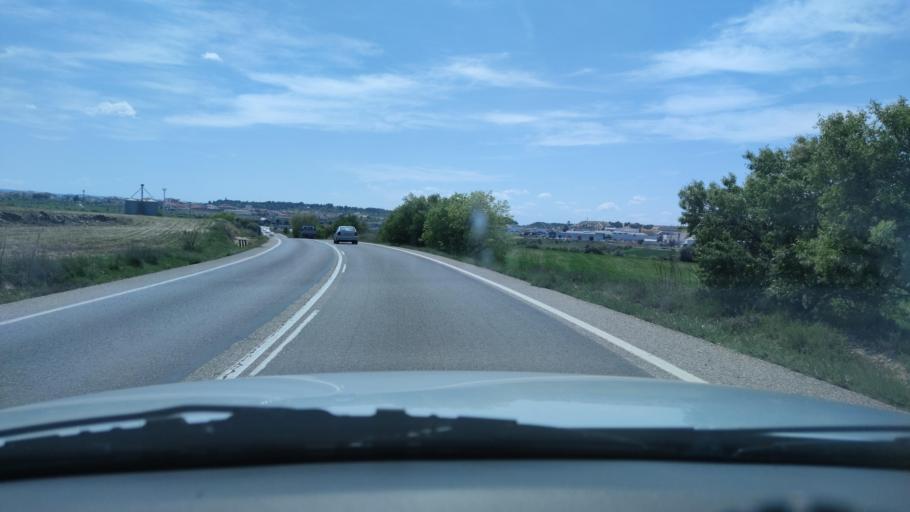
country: ES
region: Catalonia
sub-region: Provincia de Lleida
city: Tarrega
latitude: 41.6703
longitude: 1.1408
